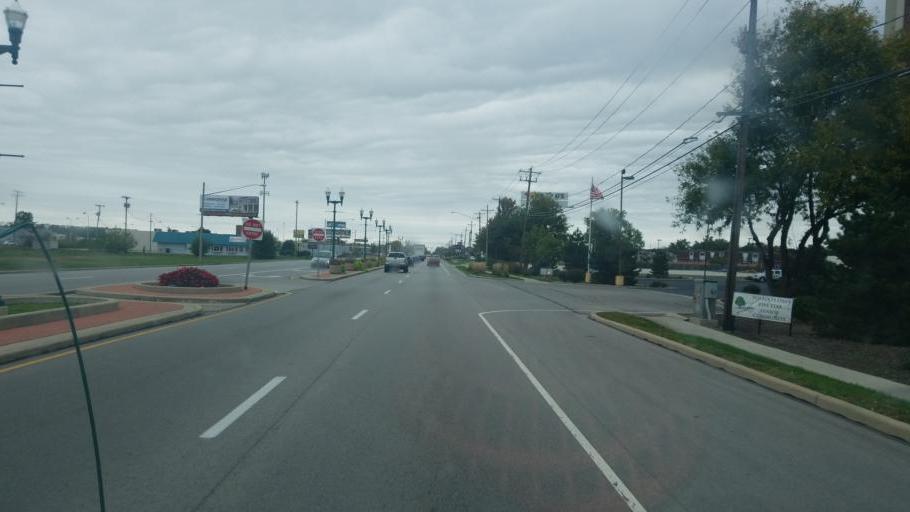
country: US
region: Ohio
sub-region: Lucas County
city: Maumee
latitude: 41.5960
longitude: -83.6645
